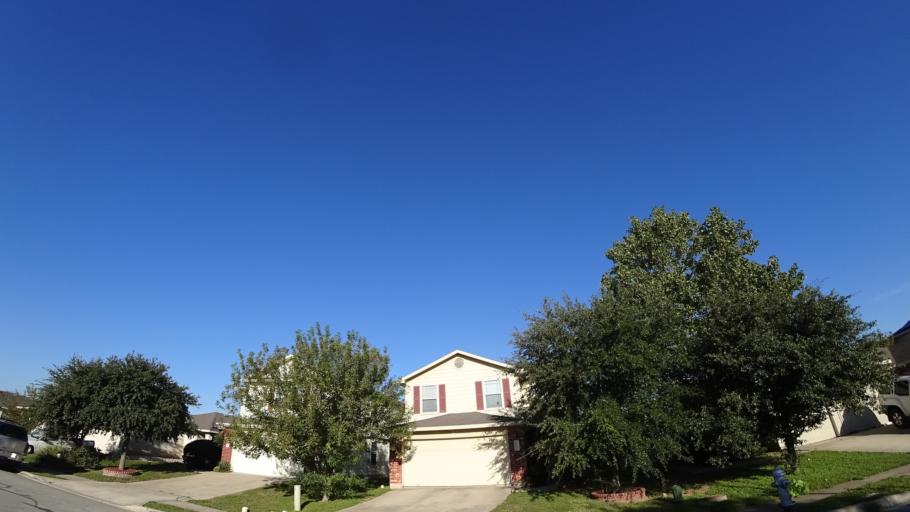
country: US
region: Texas
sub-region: Travis County
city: Austin
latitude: 30.2237
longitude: -97.6928
